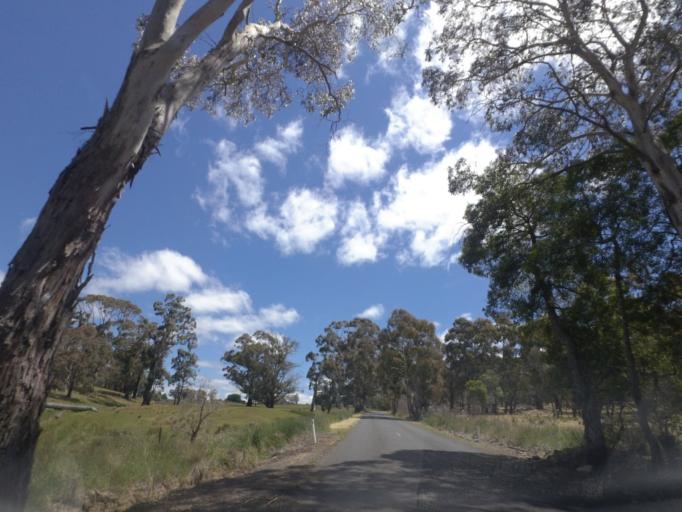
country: AU
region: Victoria
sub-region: Mount Alexander
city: Castlemaine
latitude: -37.3166
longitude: 144.1821
